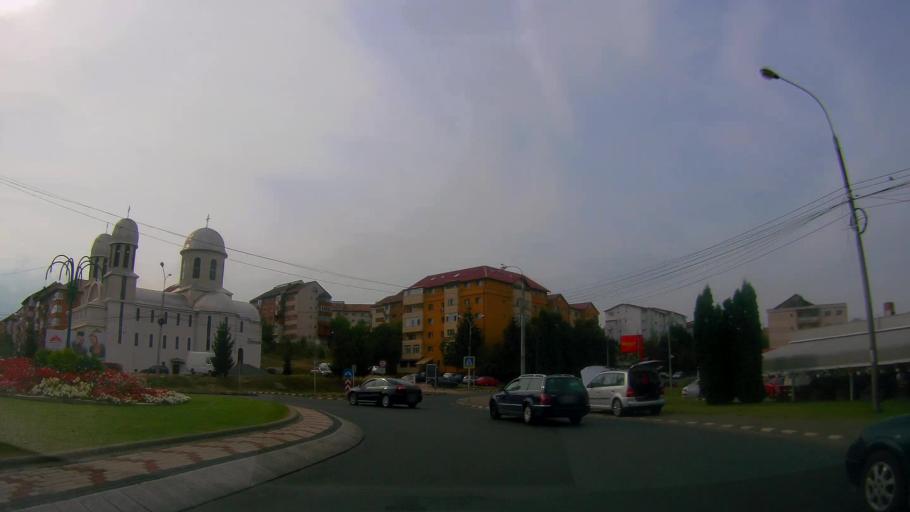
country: RO
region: Salaj
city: Zalau
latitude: 47.2031
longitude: 23.0515
